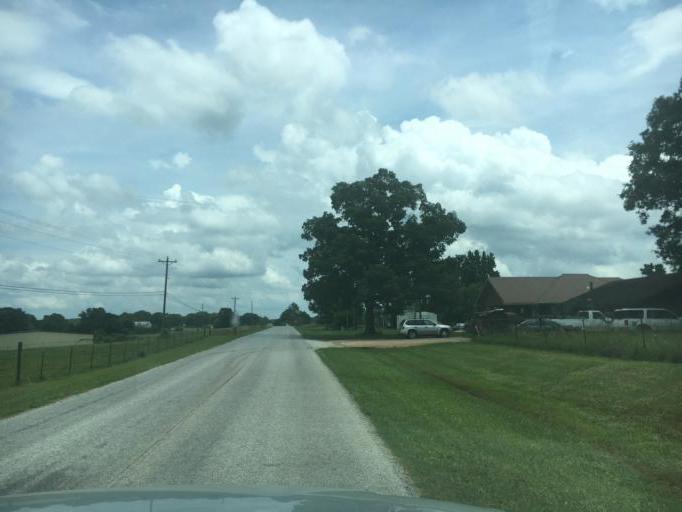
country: US
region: Georgia
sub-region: Franklin County
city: Gumlog
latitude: 34.4584
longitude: -83.0561
